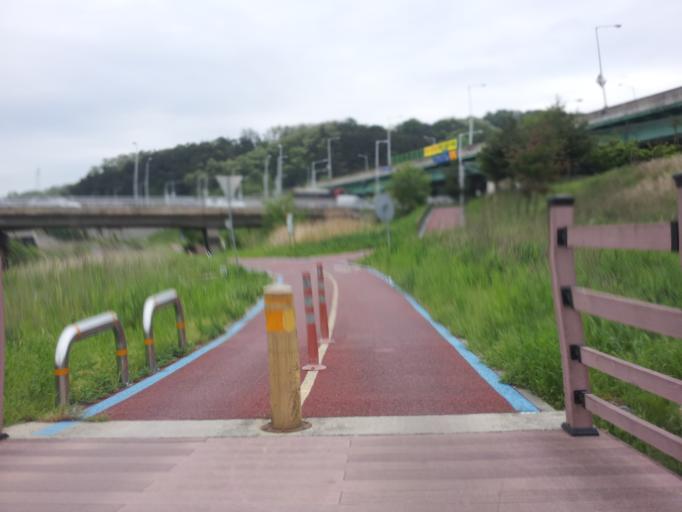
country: KR
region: Daejeon
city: Daejeon
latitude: 36.3773
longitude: 127.4099
